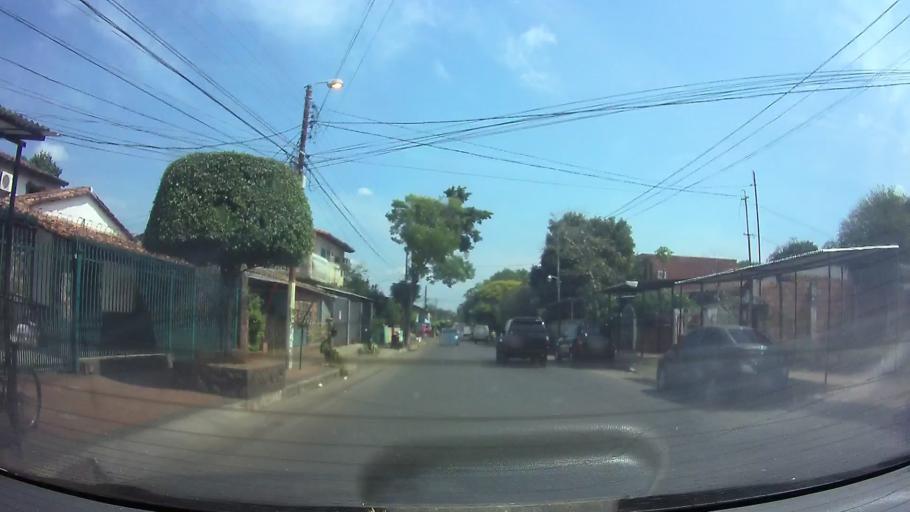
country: PY
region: Central
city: San Lorenzo
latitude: -25.3443
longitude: -57.4925
